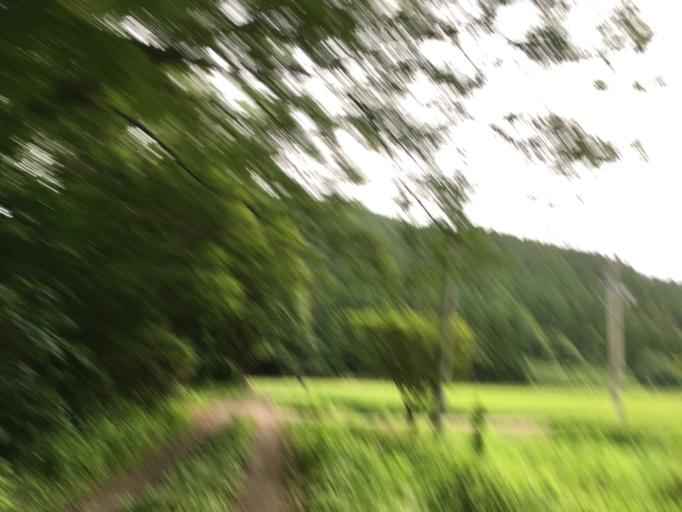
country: JP
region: Fukushima
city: Inawashiro
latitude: 37.4282
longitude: 140.0707
